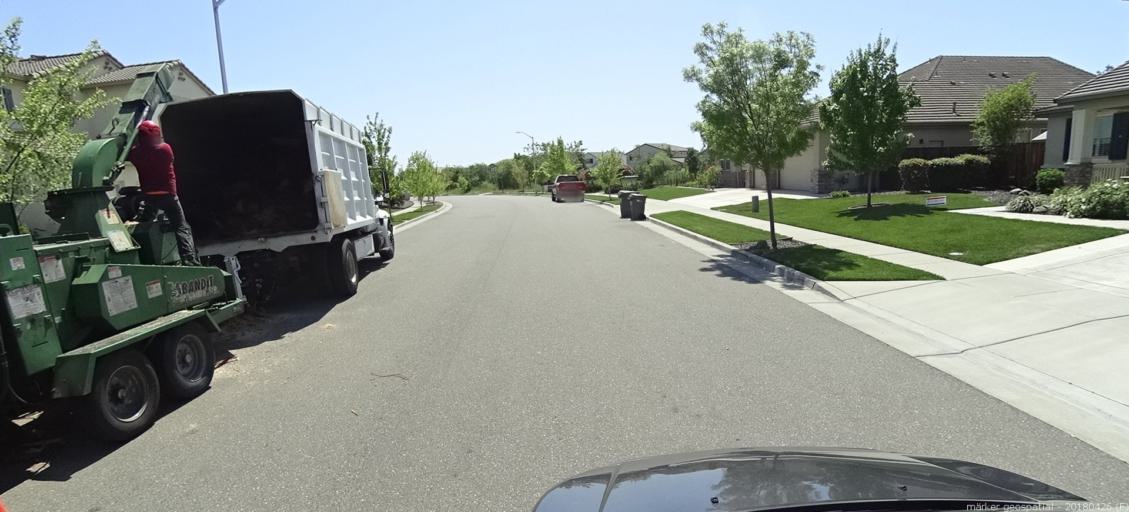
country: US
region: California
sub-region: Yolo County
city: West Sacramento
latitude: 38.5309
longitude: -121.5747
